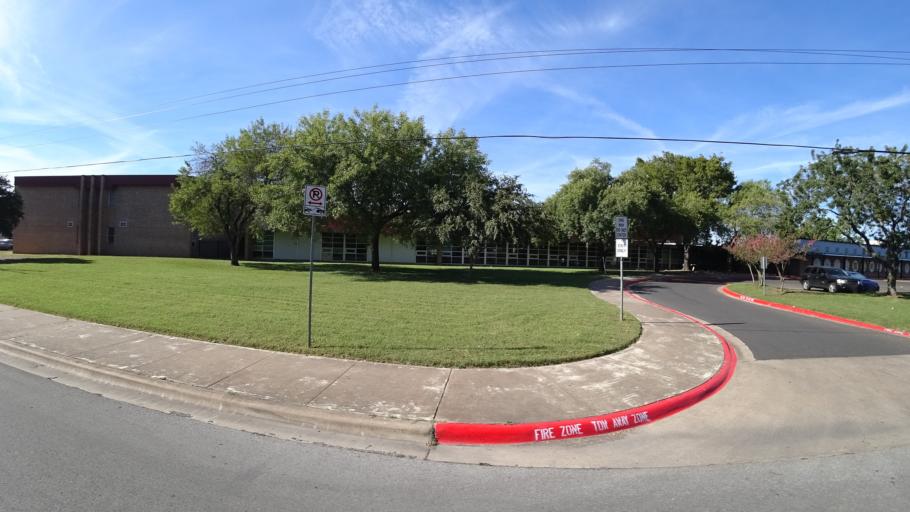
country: US
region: Texas
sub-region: Travis County
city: Austin
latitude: 30.2570
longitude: -97.6813
